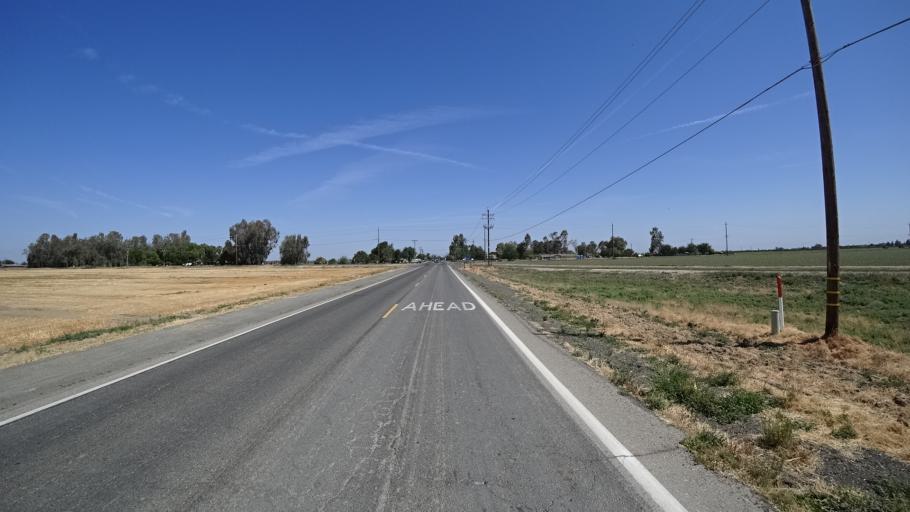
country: US
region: California
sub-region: Kings County
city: Lemoore
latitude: 36.2382
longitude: -119.7806
